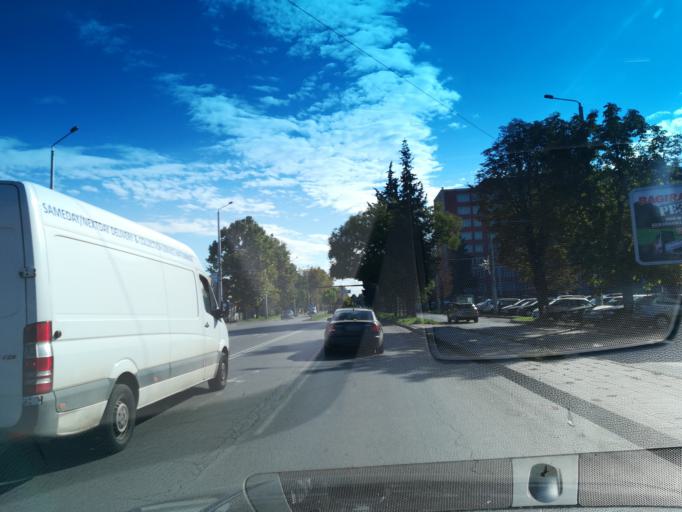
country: BG
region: Stara Zagora
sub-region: Obshtina Stara Zagora
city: Stara Zagora
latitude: 42.4136
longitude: 25.6385
